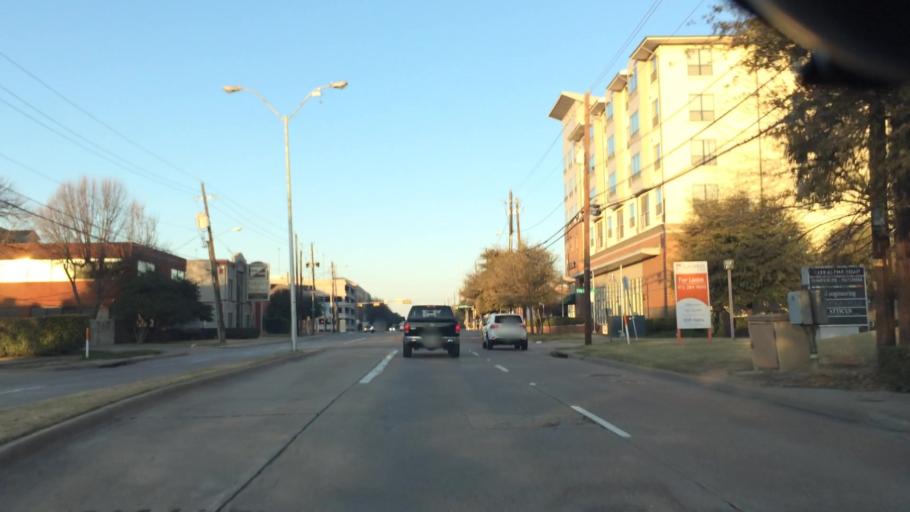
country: US
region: Texas
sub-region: Dallas County
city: Addison
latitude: 32.9329
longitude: -96.8159
